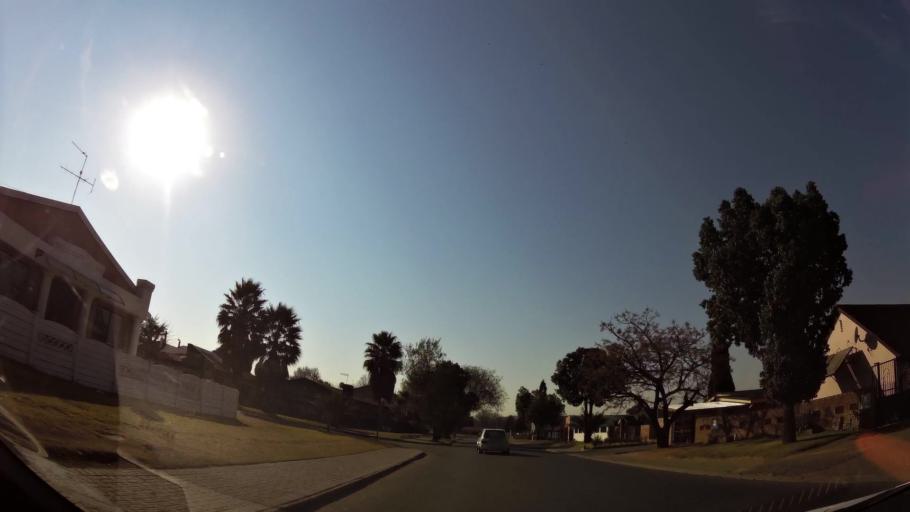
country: ZA
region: Gauteng
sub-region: Ekurhuleni Metropolitan Municipality
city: Boksburg
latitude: -26.2291
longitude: 28.2342
